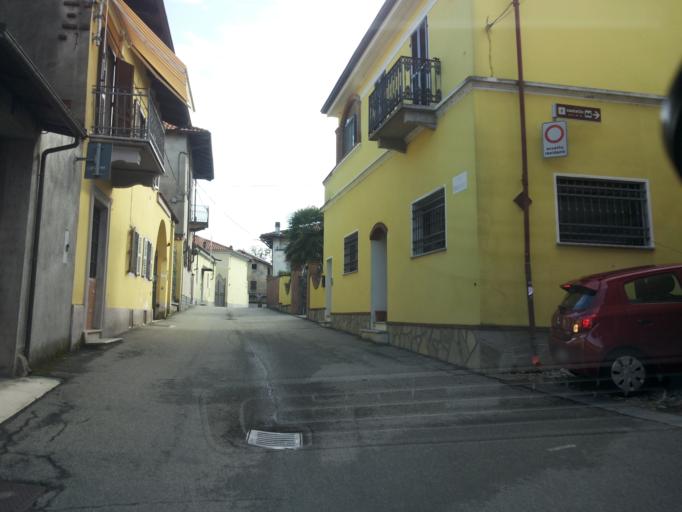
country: IT
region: Piedmont
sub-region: Provincia di Vercelli
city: Moncrivello
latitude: 45.3303
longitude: 7.9967
